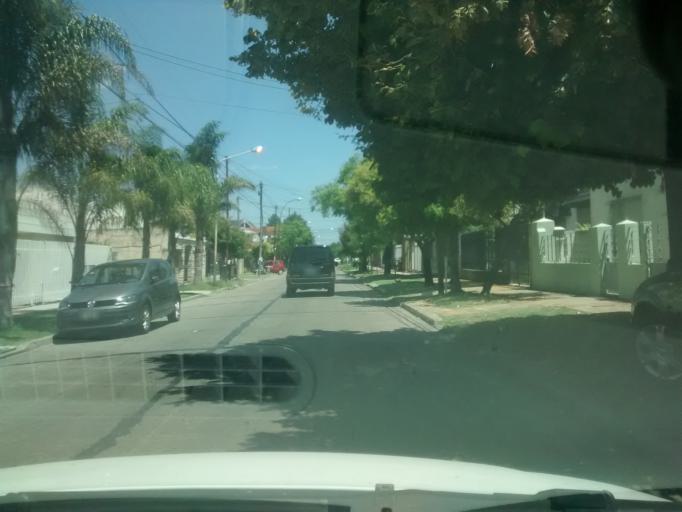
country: AR
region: Buenos Aires
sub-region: Partido de Moron
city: Moron
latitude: -34.6632
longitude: -58.6074
